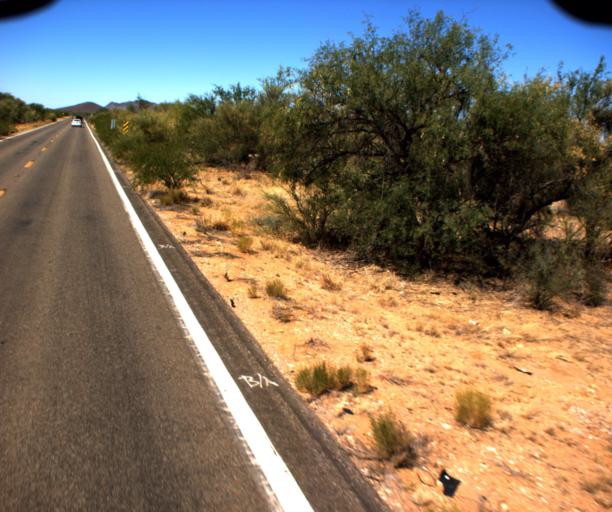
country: US
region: Arizona
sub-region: Pima County
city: Sells
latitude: 31.9399
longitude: -111.7719
